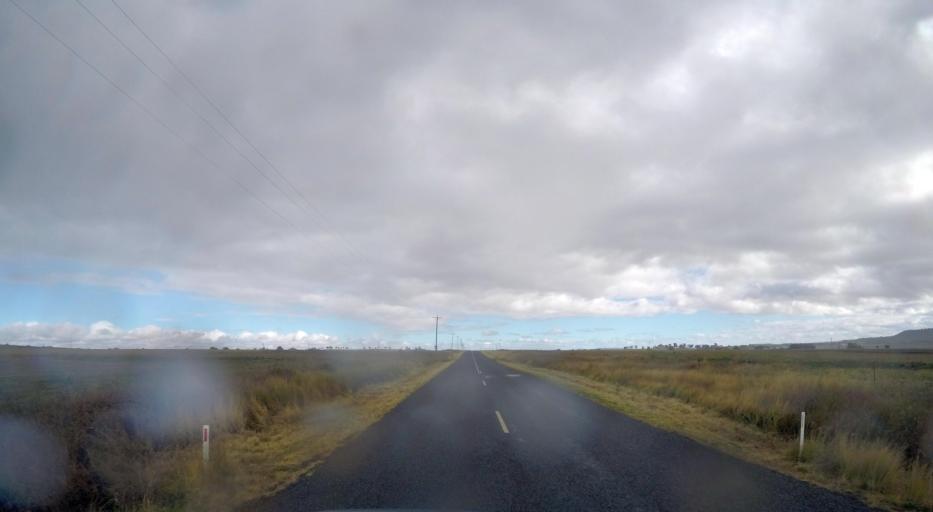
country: AU
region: Queensland
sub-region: Southern Downs
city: Warwick
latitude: -28.0523
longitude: 152.0308
